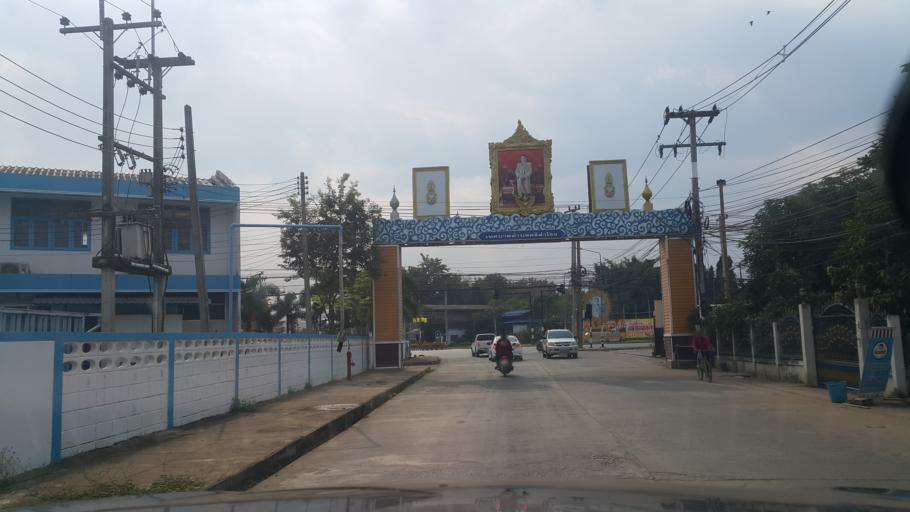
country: TH
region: Sukhothai
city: Si Samrong
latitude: 17.1636
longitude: 99.8614
